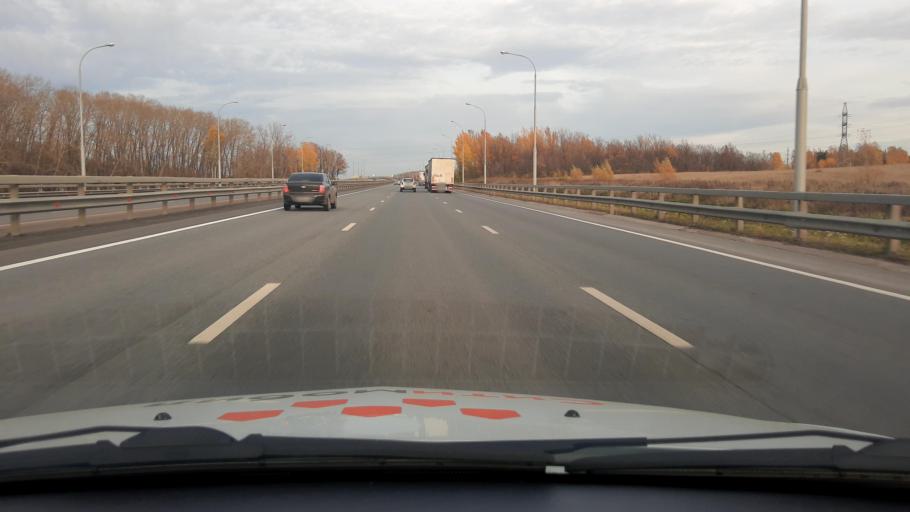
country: RU
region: Bashkortostan
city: Kabakovo
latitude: 54.6513
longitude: 56.0977
